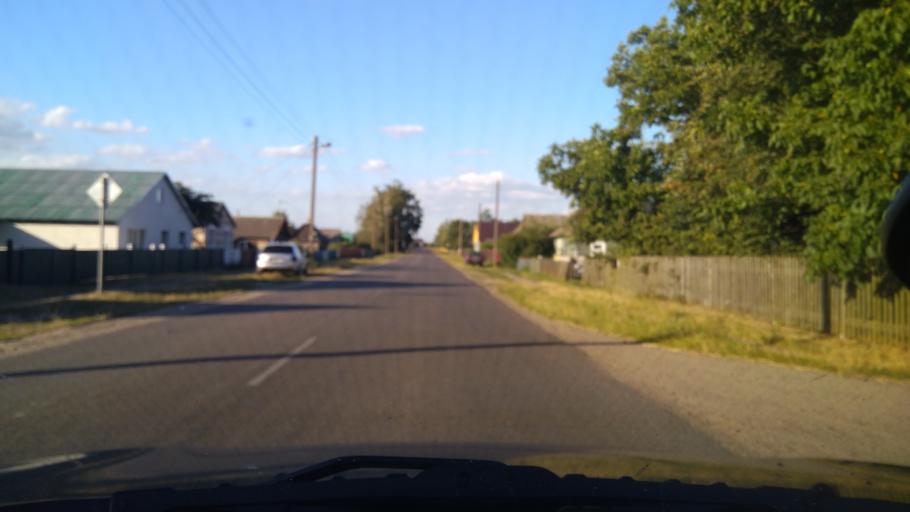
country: BY
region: Brest
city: Byaroza
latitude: 52.5862
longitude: 24.8666
